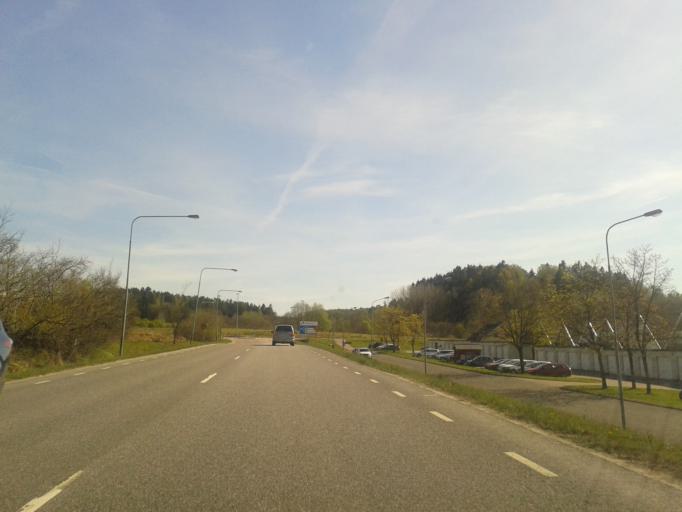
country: SE
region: Vaestra Goetaland
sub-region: Ale Kommun
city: Nodinge-Nol
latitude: 57.8925
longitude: 12.0677
